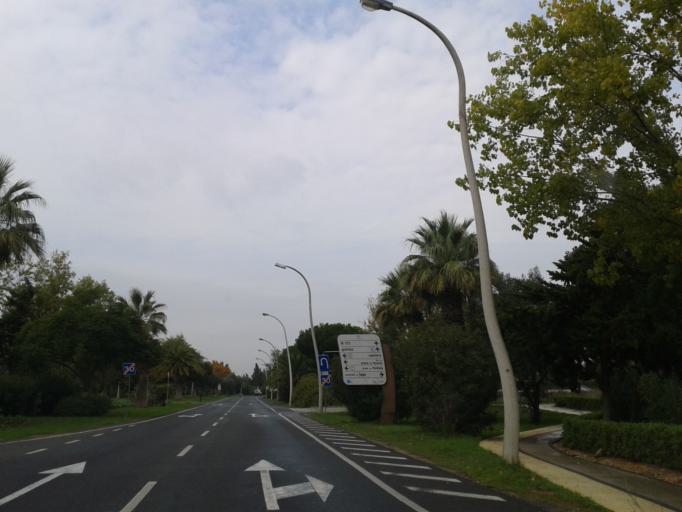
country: PT
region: Faro
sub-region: Loule
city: Vilamoura
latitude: 37.0904
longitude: -8.1237
